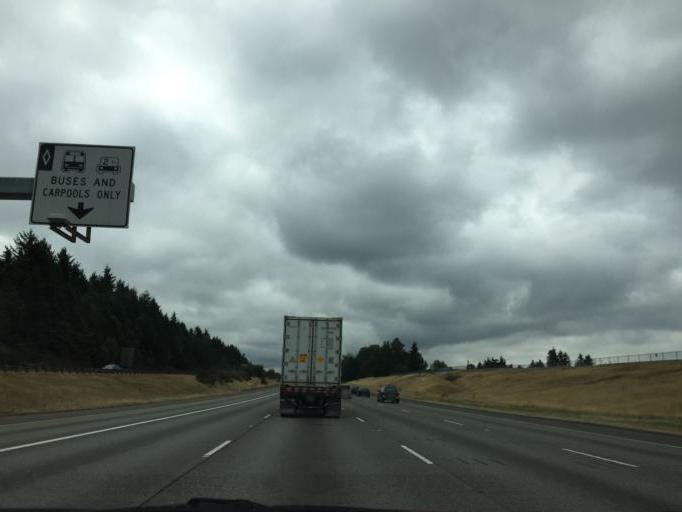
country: US
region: Washington
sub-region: King County
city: Des Moines
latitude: 47.3793
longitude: -122.2913
